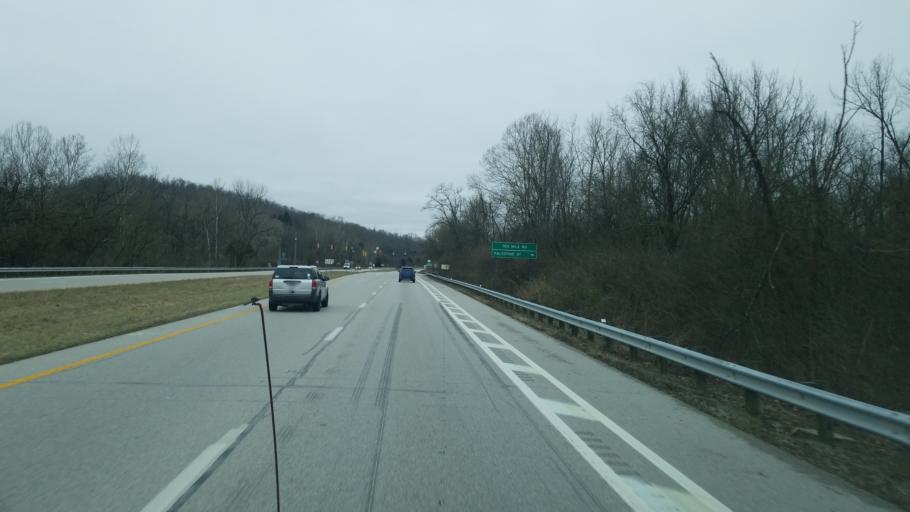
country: US
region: Ohio
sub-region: Clermont County
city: Withamsville
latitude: 39.0111
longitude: -84.3045
